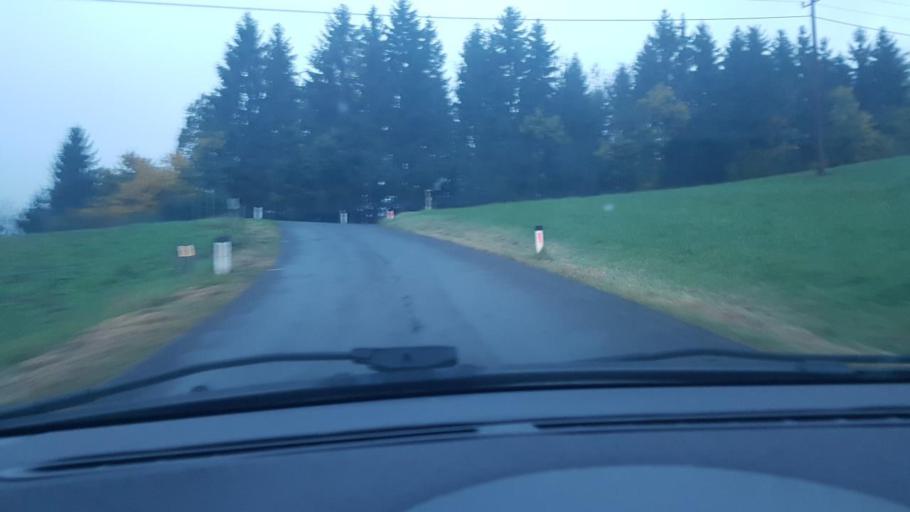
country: AT
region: Styria
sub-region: Politischer Bezirk Leibnitz
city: Sulztal an der Weinstrasse
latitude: 46.6602
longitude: 15.5413
